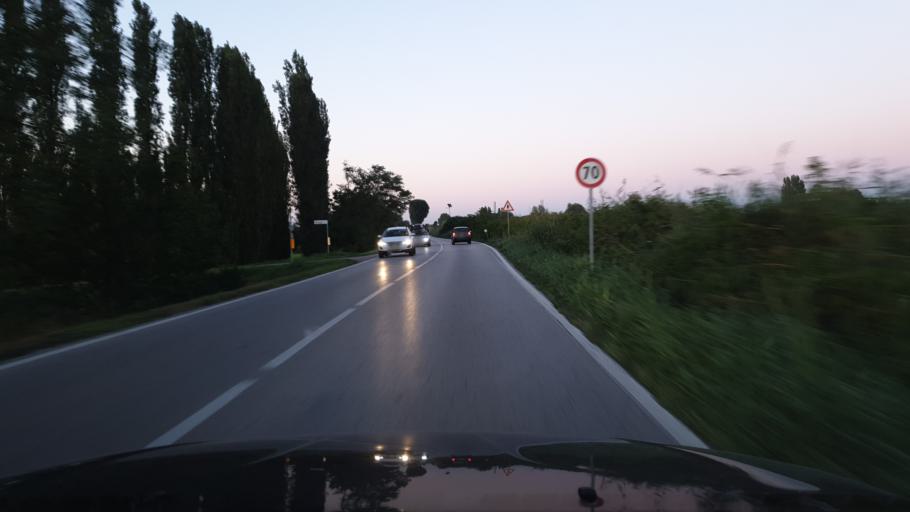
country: IT
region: Emilia-Romagna
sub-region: Provincia di Bologna
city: Altedo
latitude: 44.6538
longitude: 11.4857
